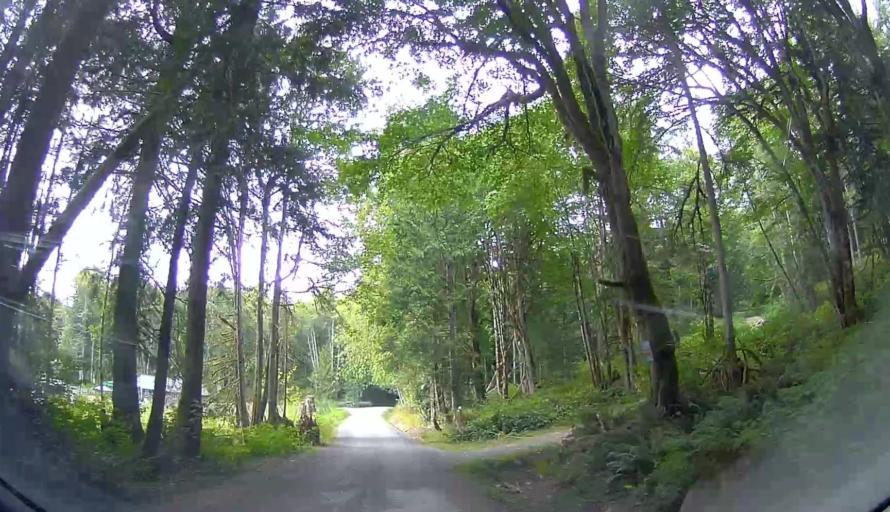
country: US
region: Washington
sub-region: Skagit County
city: Burlington
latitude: 48.5916
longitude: -122.3922
